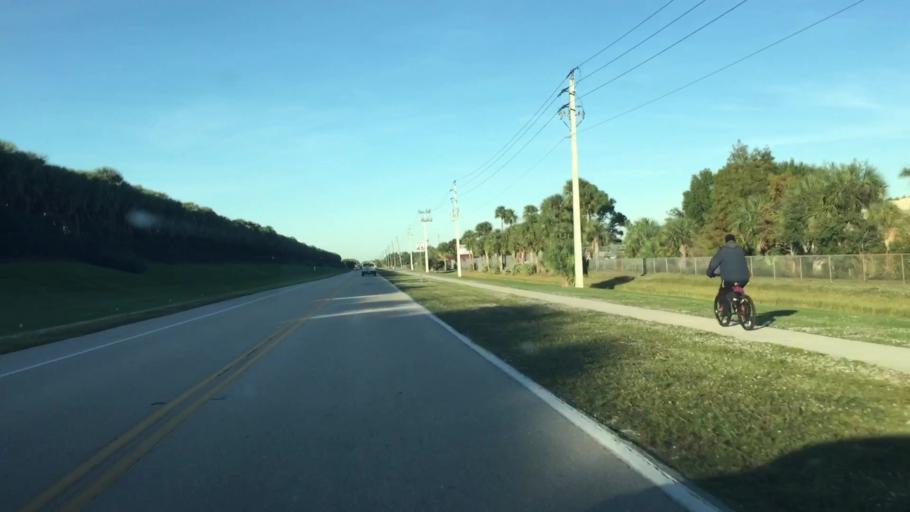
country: US
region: Florida
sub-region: Lee County
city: Estero
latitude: 26.4204
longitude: -81.7949
